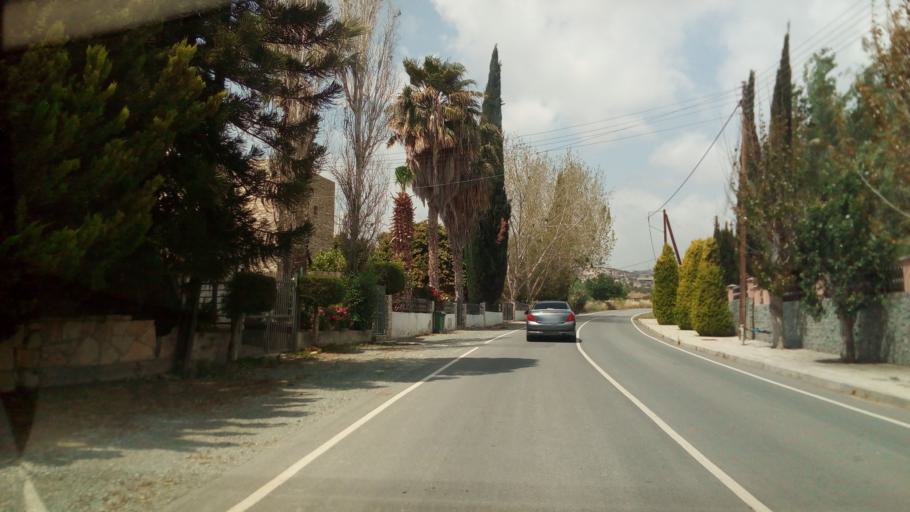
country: CY
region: Limassol
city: Pissouri
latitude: 34.6712
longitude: 32.7230
